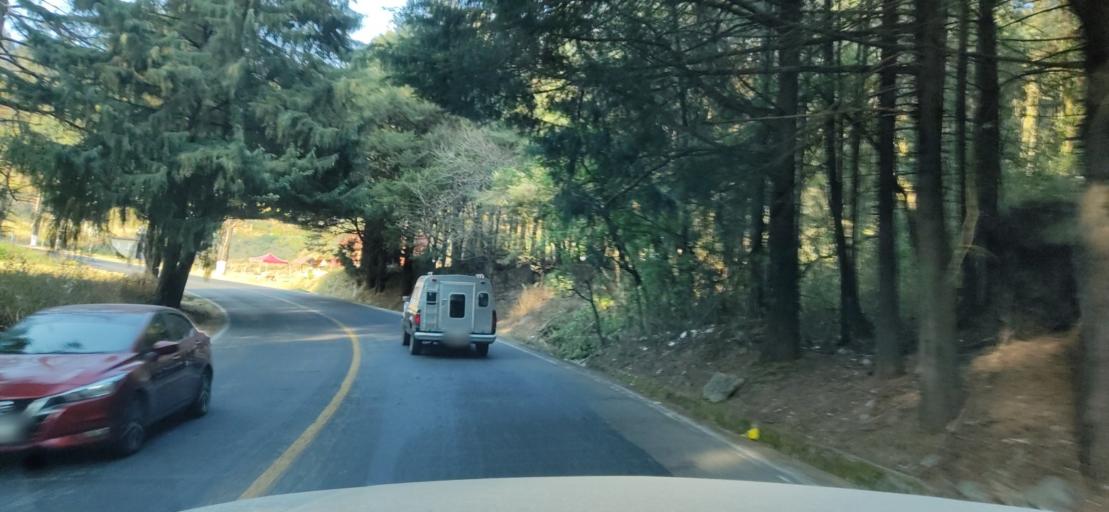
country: MX
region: Mexico
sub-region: Ocoyoacac
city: San Jeronimo Acazulco
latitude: 19.2442
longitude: -99.3715
